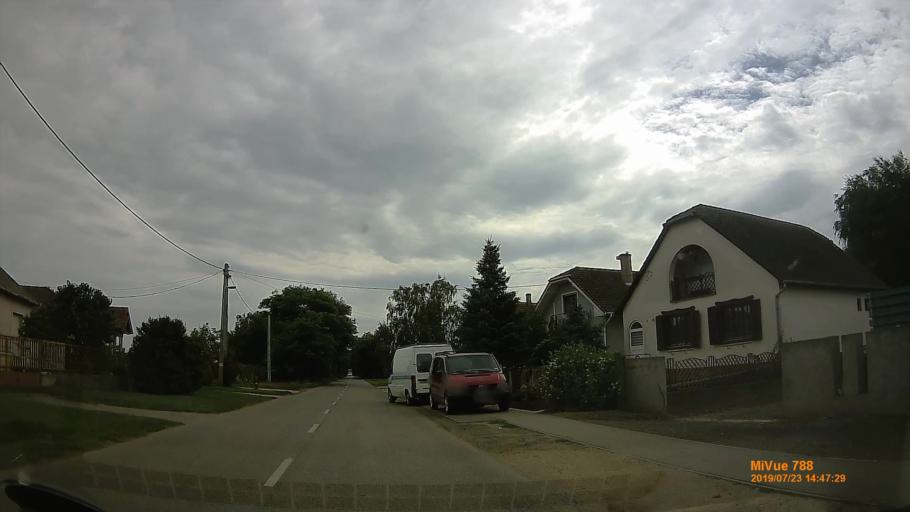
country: HU
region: Szabolcs-Szatmar-Bereg
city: Nyiregyhaza
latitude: 47.9108
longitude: 21.6745
